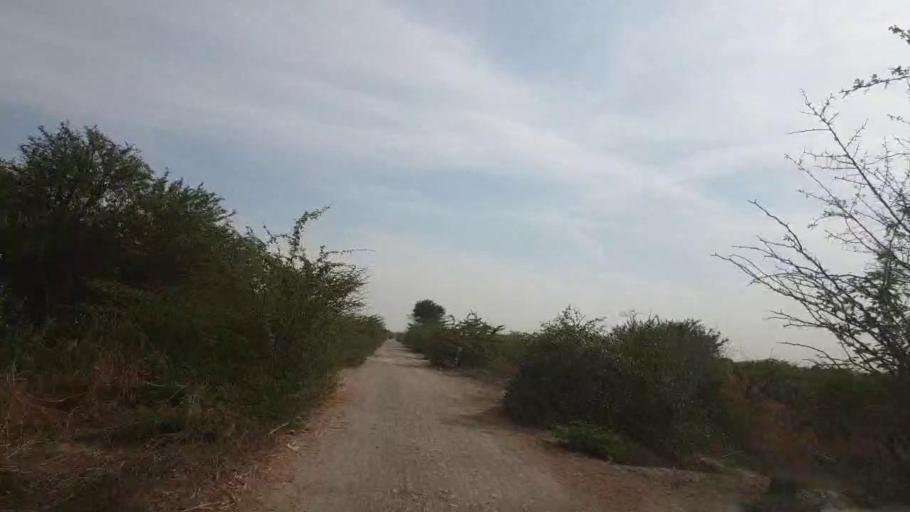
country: PK
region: Sindh
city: Nabisar
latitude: 25.0172
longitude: 69.5622
